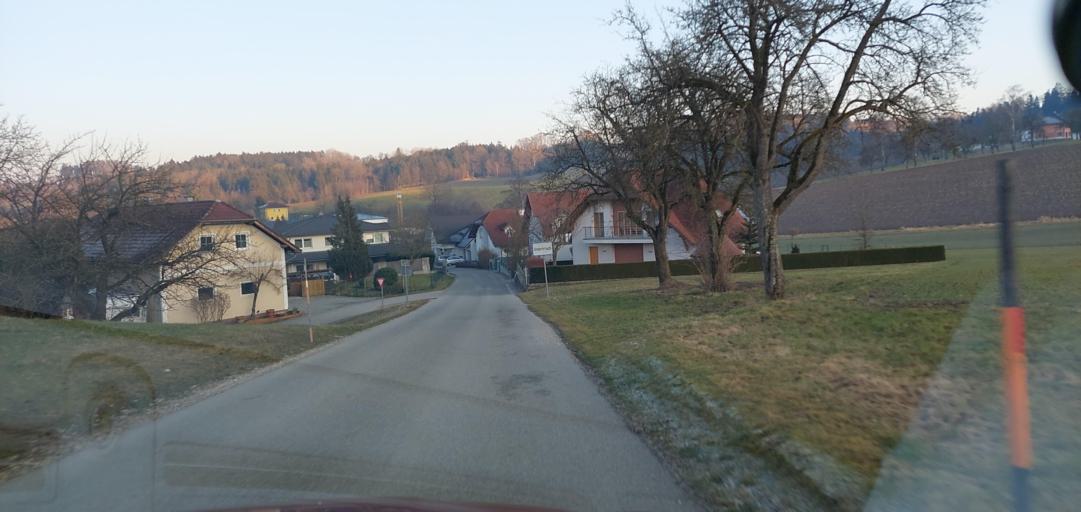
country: AT
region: Upper Austria
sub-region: Politischer Bezirk Grieskirchen
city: Bad Schallerbach
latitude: 48.1827
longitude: 13.9143
